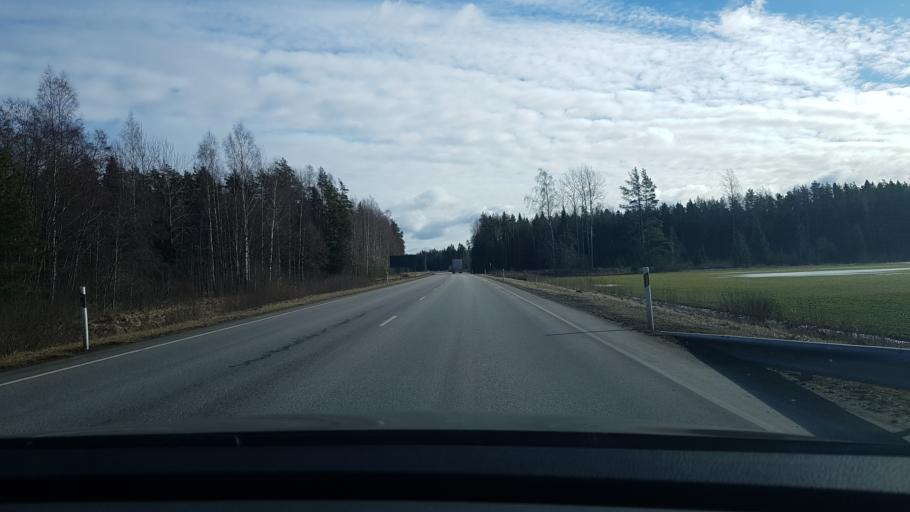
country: EE
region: Paernumaa
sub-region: Saarde vald
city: Kilingi-Nomme
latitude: 58.1678
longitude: 24.8217
